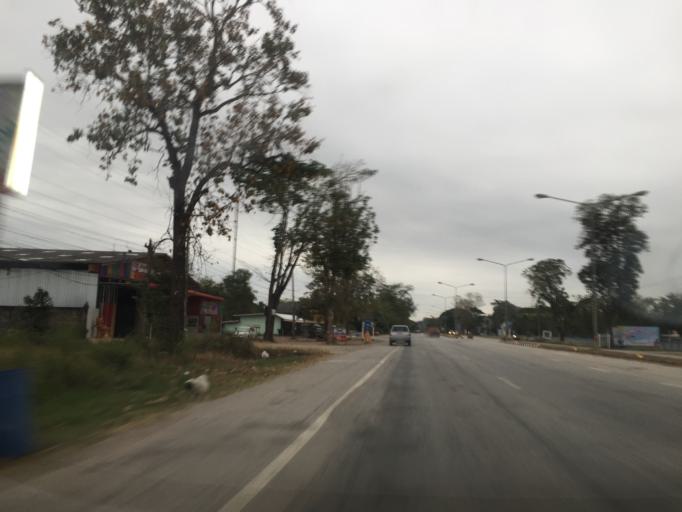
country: TH
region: Loei
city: Erawan
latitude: 17.3071
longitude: 101.9493
